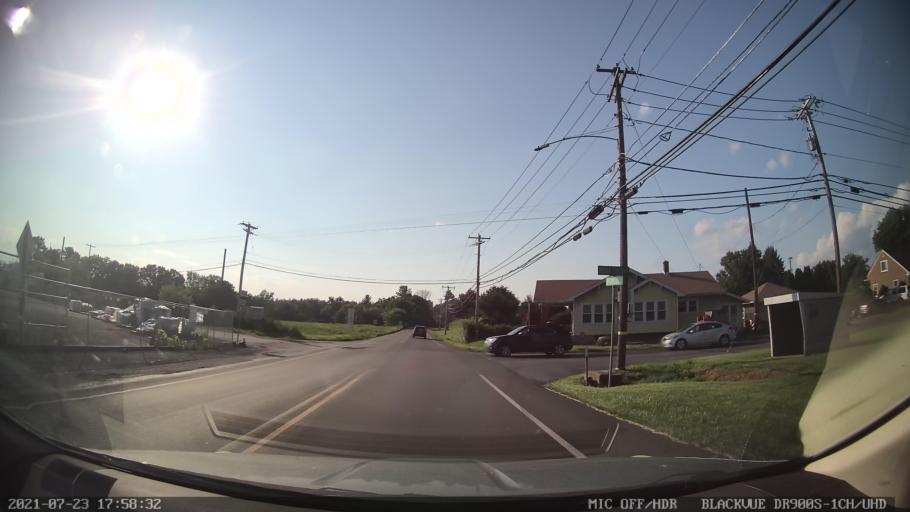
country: US
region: Pennsylvania
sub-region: Lehigh County
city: Macungie
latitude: 40.5207
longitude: -75.5468
